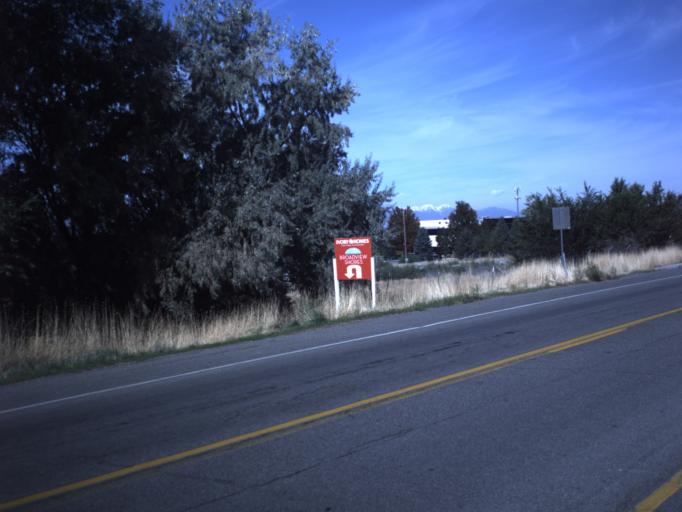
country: US
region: Utah
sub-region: Utah County
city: Orem
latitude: 40.2733
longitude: -111.7257
